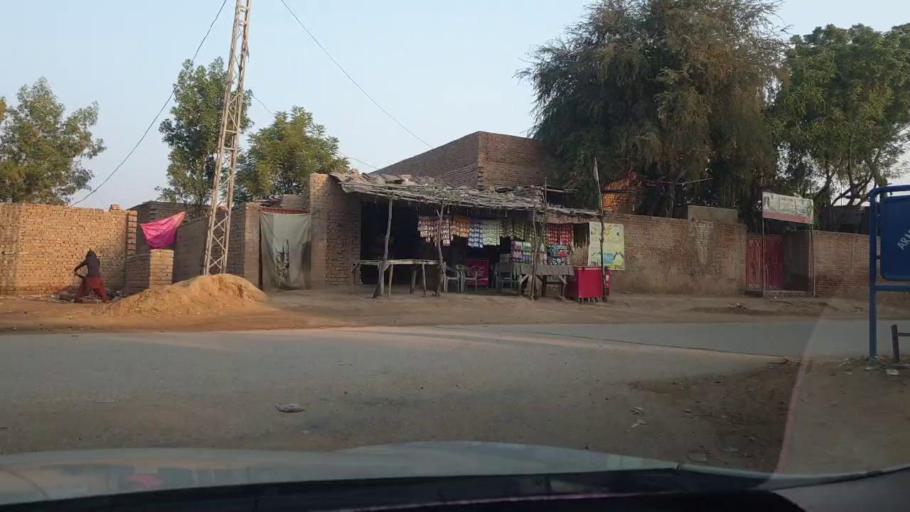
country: PK
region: Sindh
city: Sehwan
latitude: 26.3982
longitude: 67.8609
